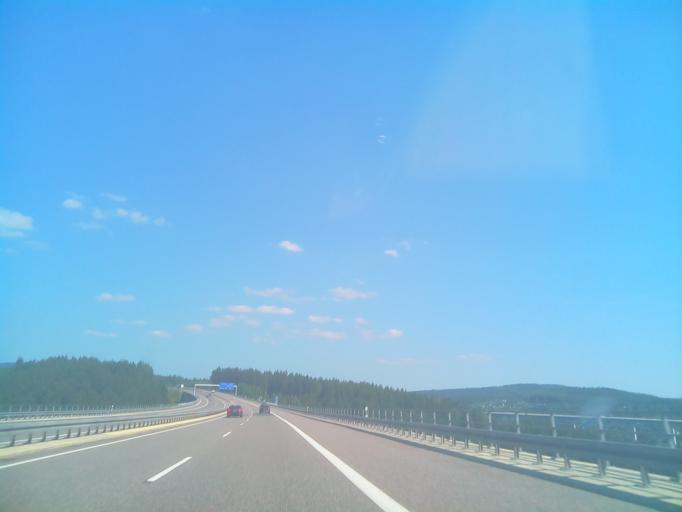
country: DE
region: Thuringia
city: Benshausen
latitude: 50.6105
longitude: 10.6314
